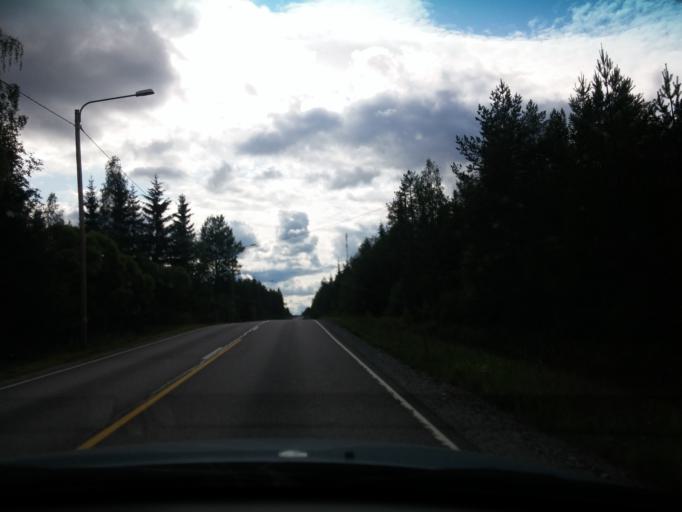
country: FI
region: Central Finland
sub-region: Saarijaervi-Viitasaari
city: Pylkoenmaeki
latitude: 62.6332
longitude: 24.8086
